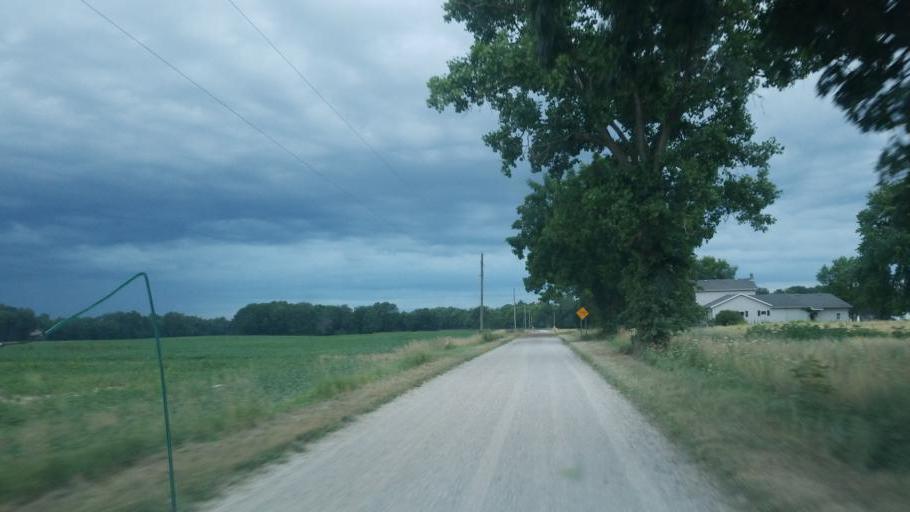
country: US
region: Ohio
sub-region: Defiance County
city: Hicksville
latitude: 41.3282
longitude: -84.8454
